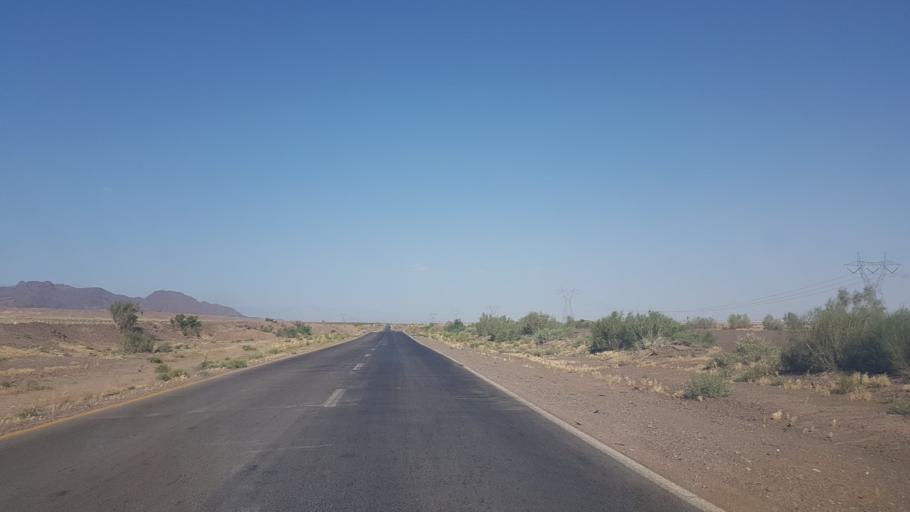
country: IR
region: Razavi Khorasan
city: Joghatay
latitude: 36.3629
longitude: 56.6115
